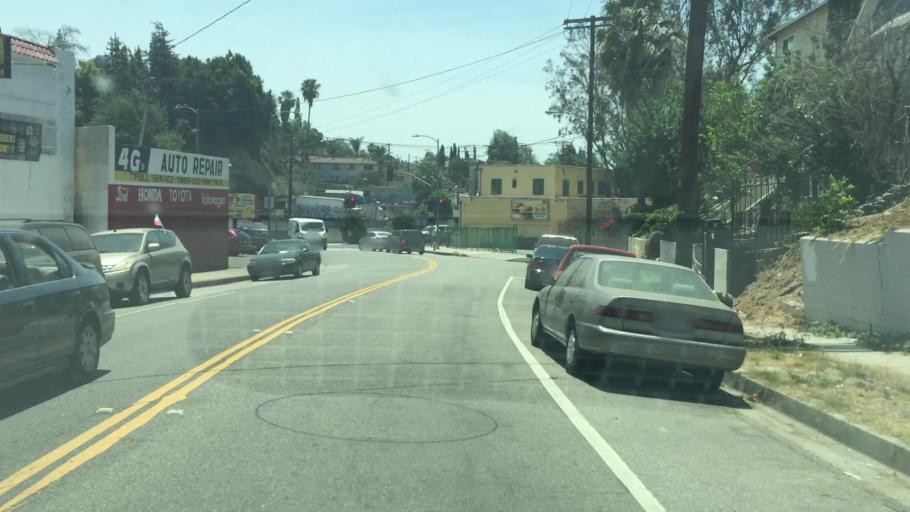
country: US
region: California
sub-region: Los Angeles County
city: Glendale
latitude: 34.1137
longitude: -118.2085
